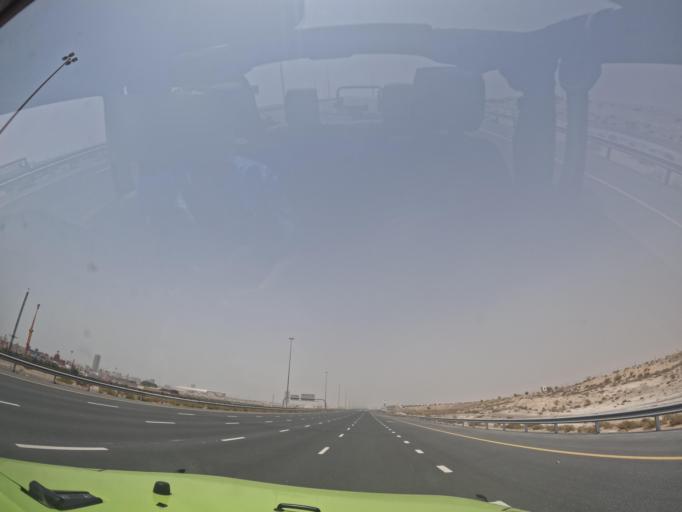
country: AE
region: Dubai
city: Dubai
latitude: 25.0617
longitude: 55.3087
